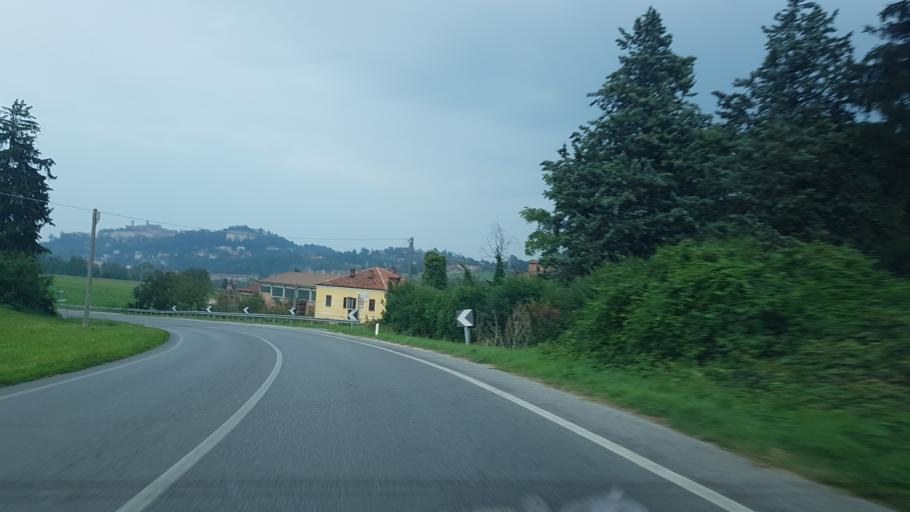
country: IT
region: Piedmont
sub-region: Provincia di Cuneo
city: Mondovi
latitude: 44.3721
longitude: 7.8055
